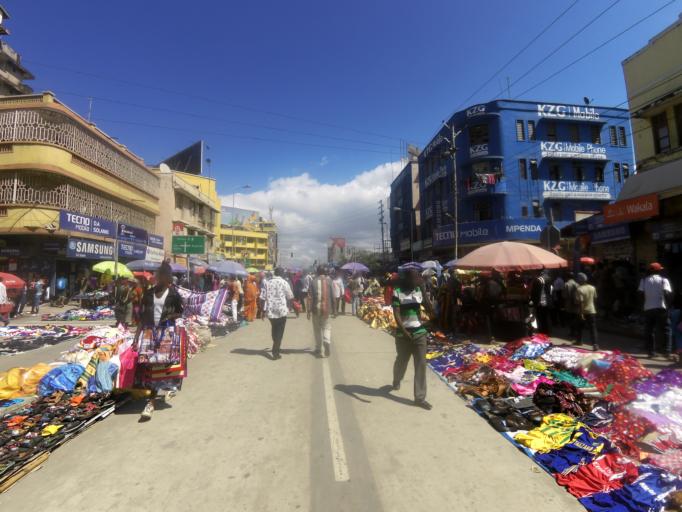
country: TZ
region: Dar es Salaam
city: Dar es Salaam
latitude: -6.8231
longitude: 39.2736
